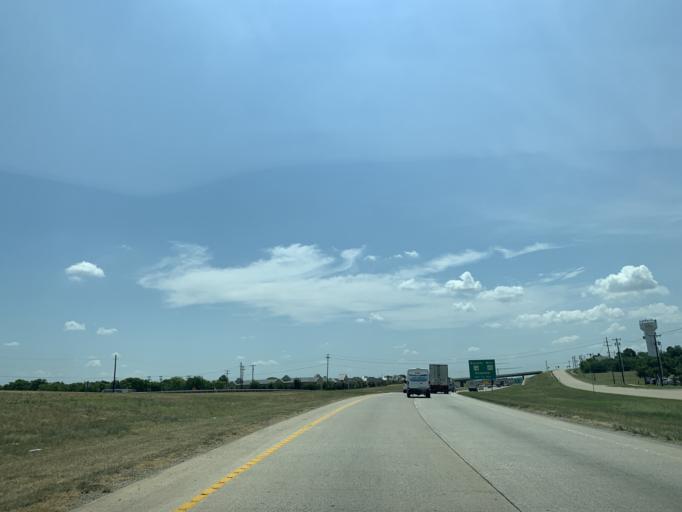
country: US
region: Texas
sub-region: Denton County
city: Roanoke
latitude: 33.0097
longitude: -97.2203
